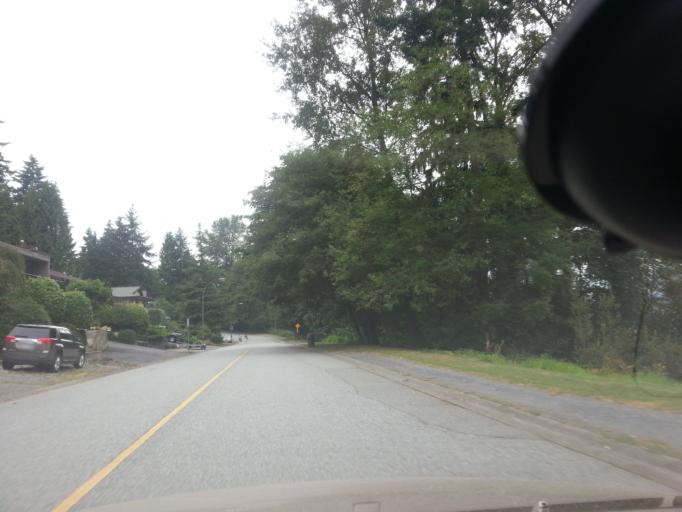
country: CA
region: British Columbia
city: Port Moody
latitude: 49.2875
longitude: -122.8729
